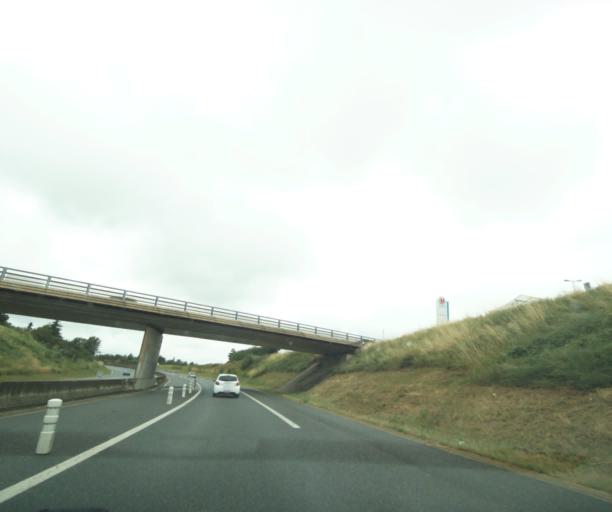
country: FR
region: Midi-Pyrenees
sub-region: Departement de l'Aveyron
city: Olemps
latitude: 44.3253
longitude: 2.5570
